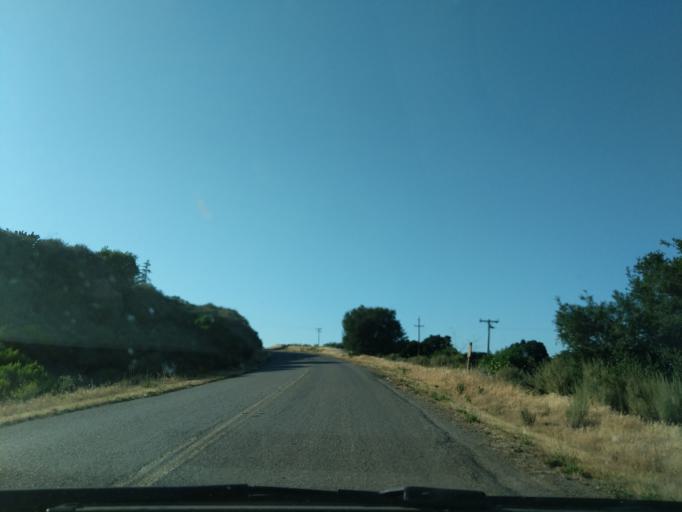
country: US
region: California
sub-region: Monterey County
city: Soledad
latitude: 36.4255
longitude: -121.4017
